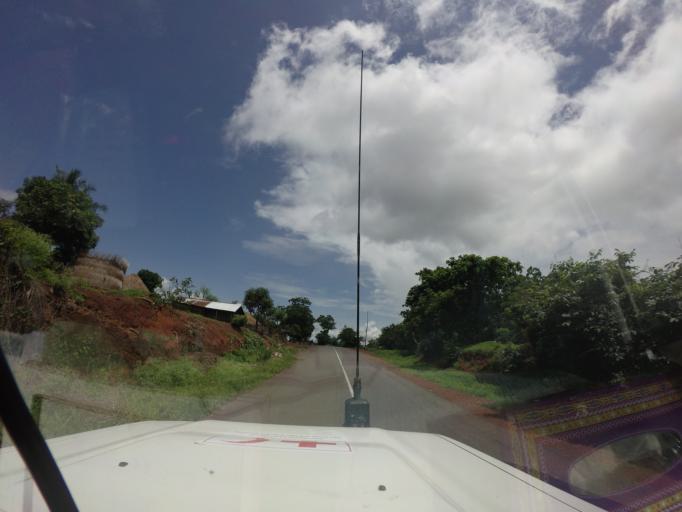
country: GN
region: Faranah
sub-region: Faranah Prefecture
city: Faranah
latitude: 10.0208
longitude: -10.8308
